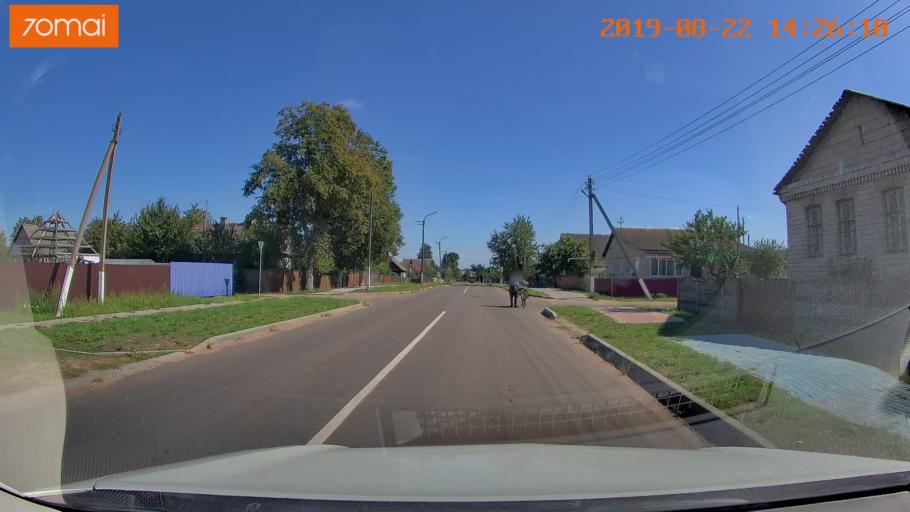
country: BY
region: Mogilev
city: Asipovichy
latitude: 53.2998
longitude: 28.6139
